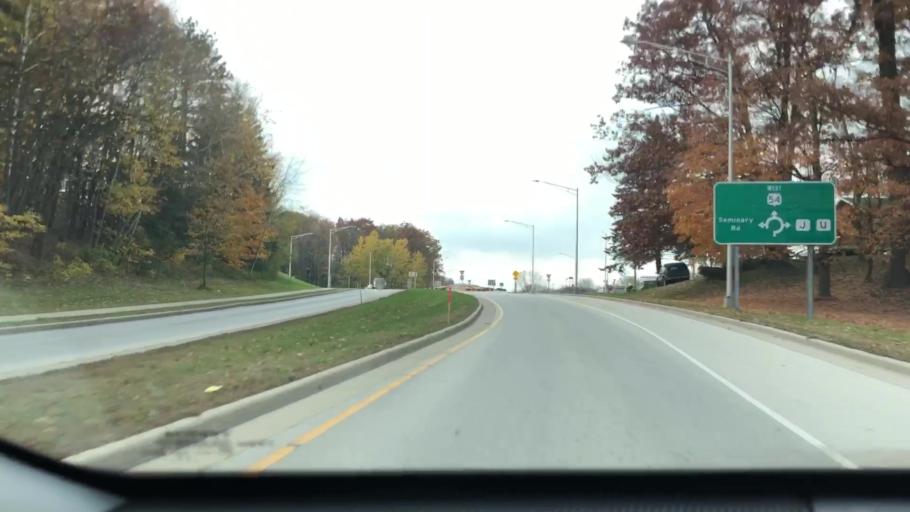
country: US
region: Wisconsin
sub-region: Brown County
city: Oneida
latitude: 44.5008
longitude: -88.1917
